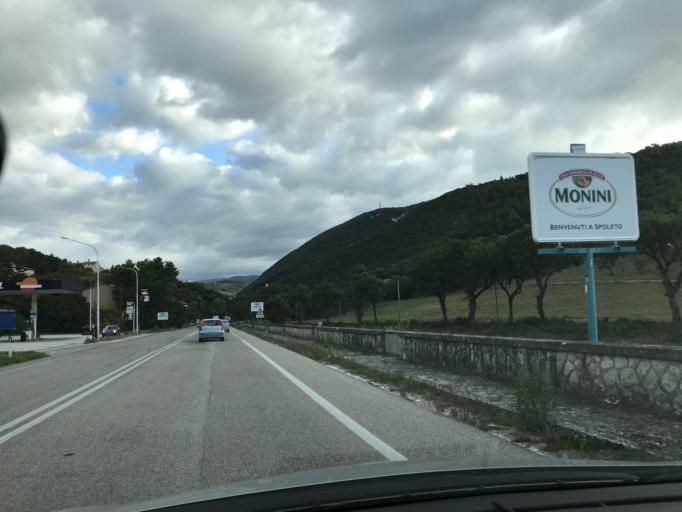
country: IT
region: Umbria
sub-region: Provincia di Perugia
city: Spoleto
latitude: 42.7198
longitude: 12.7289
